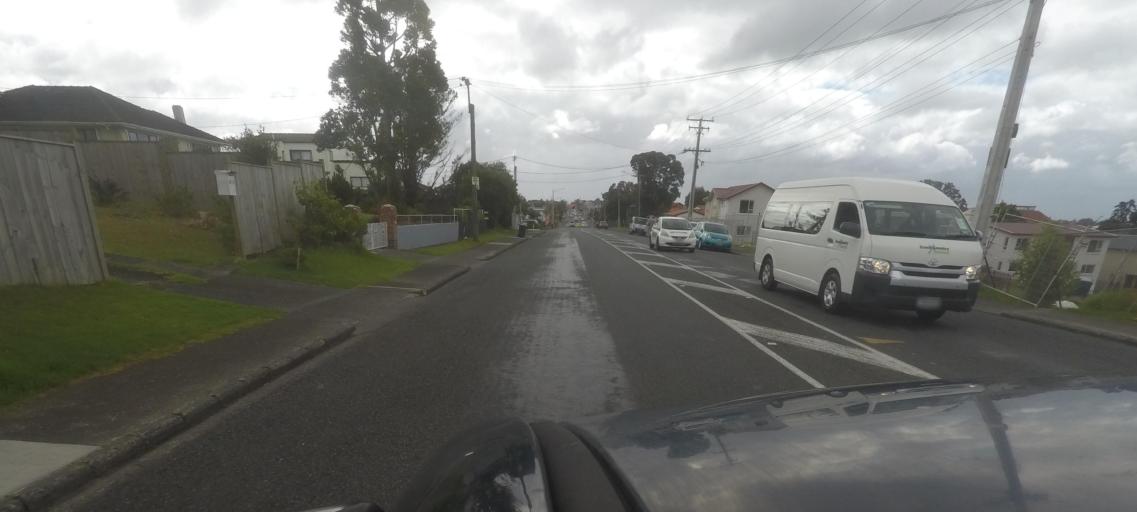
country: NZ
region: Auckland
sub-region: Auckland
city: Auckland
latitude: -36.9165
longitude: 174.7316
